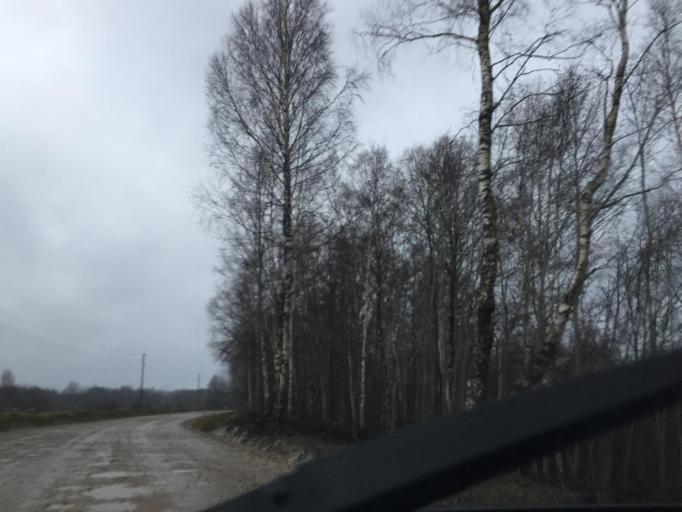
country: LV
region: Salacgrivas
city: Salacgriva
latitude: 57.7563
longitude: 24.4529
